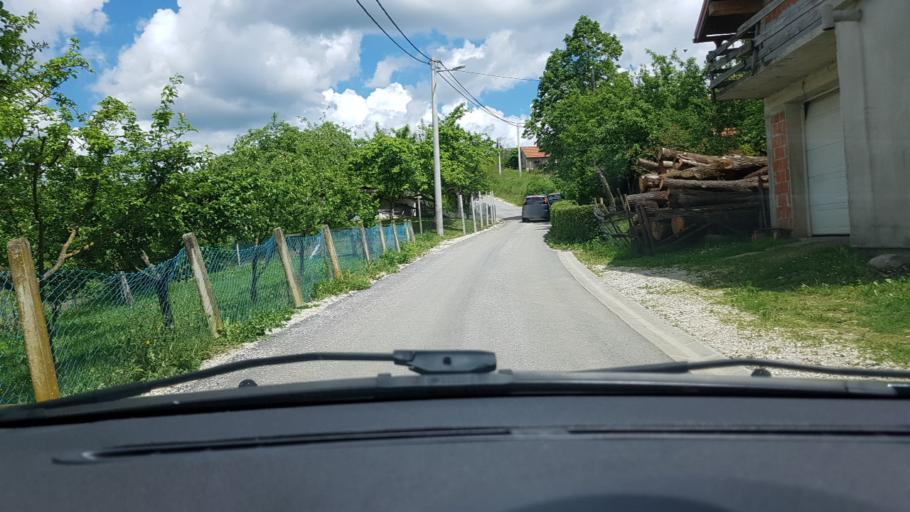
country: HR
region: Krapinsko-Zagorska
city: Pregrada
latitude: 46.1664
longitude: 15.8112
